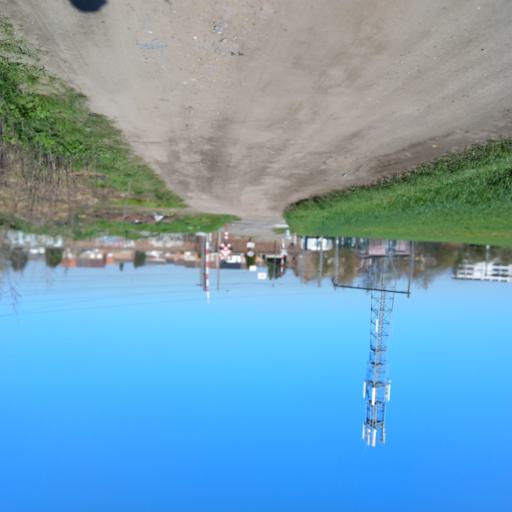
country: BE
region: Wallonia
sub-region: Province du Hainaut
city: Mons
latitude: 50.4738
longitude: 3.9659
